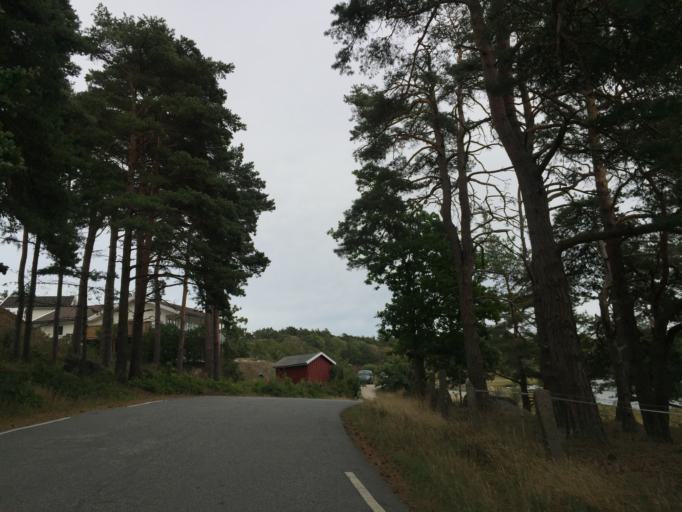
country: NO
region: Ostfold
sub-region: Hvaler
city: Skjaerhalden
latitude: 59.0463
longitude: 11.0392
